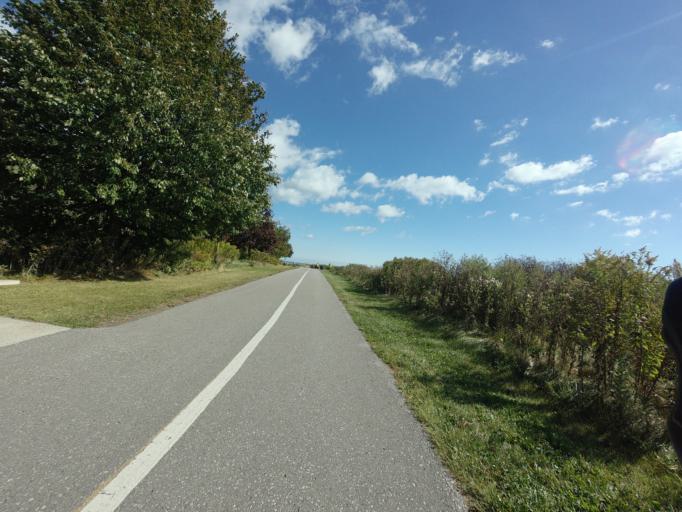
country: CA
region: Ontario
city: Ajax
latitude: 43.8161
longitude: -79.0253
